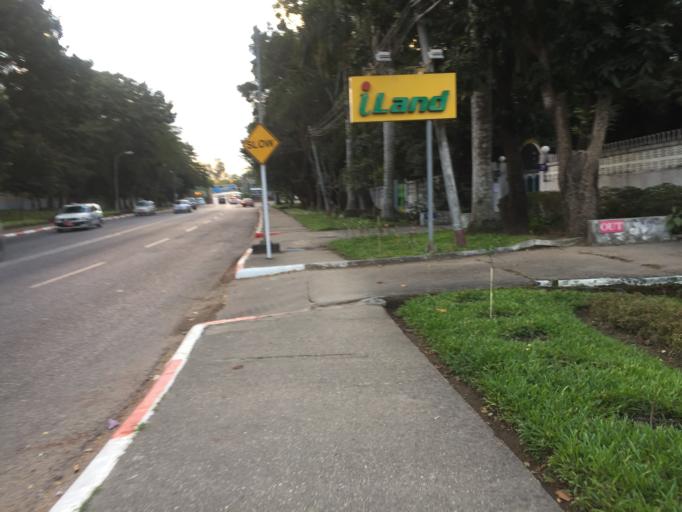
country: MM
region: Yangon
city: Yangon
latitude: 16.8908
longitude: 96.1318
